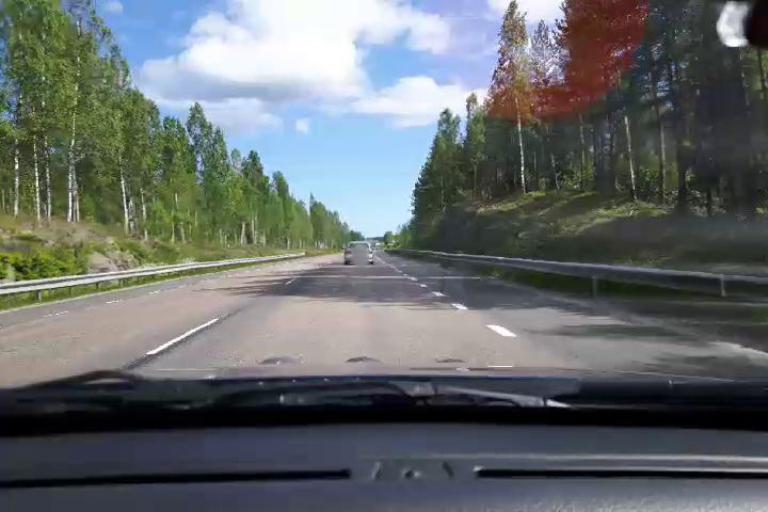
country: SE
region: Gaevleborg
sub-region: Hudiksvalls Kommun
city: Sorforsa
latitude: 61.7189
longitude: 17.0257
